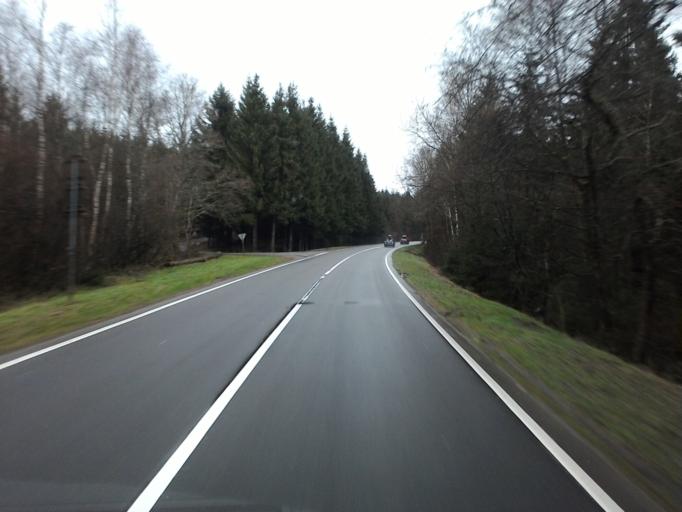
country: BE
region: Wallonia
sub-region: Province de Liege
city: Stavelot
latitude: 50.4306
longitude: 5.9291
